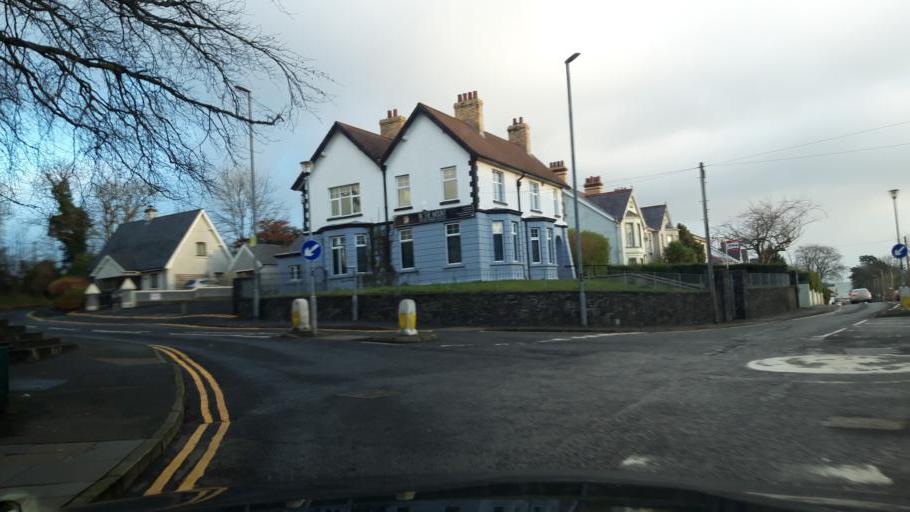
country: GB
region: Northern Ireland
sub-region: Moyle District
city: Ballycastle
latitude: 55.2025
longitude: -6.2471
